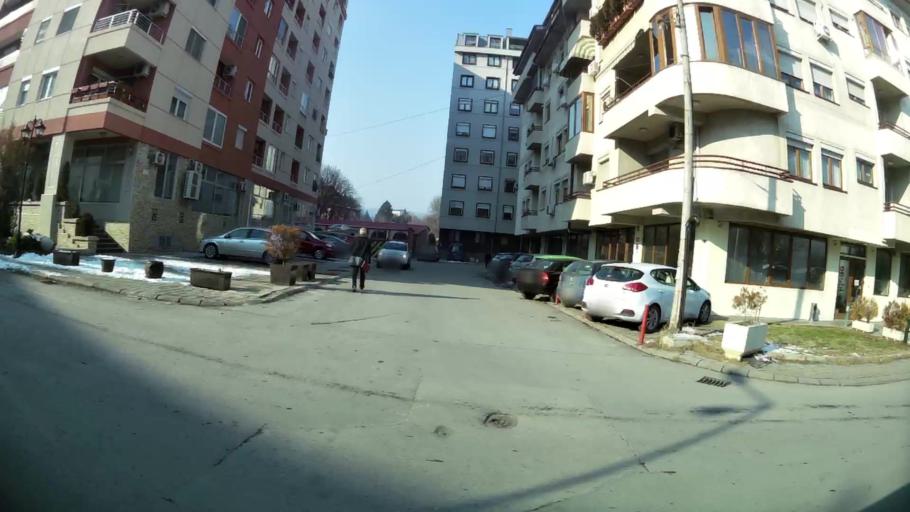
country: MK
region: Karpos
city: Skopje
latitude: 41.9872
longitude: 21.4275
